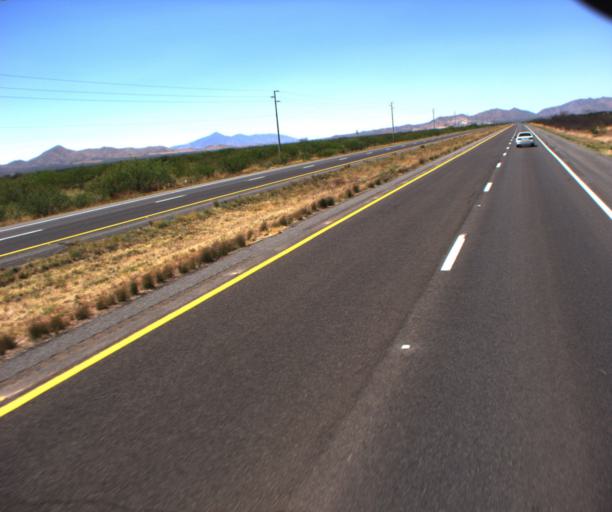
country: US
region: Arizona
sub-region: Cochise County
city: Pirtleville
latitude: 31.3611
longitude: -109.6665
